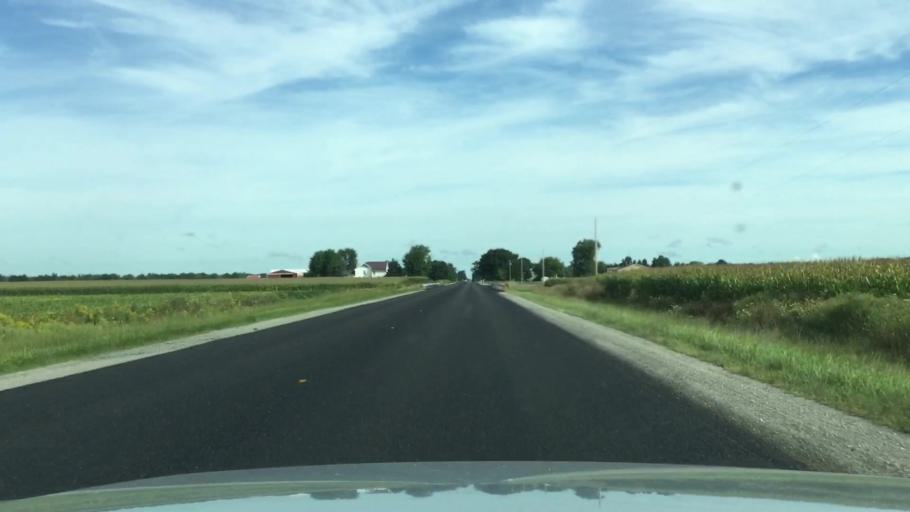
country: US
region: Michigan
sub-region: Genesee County
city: Montrose
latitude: 43.1339
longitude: -83.9291
